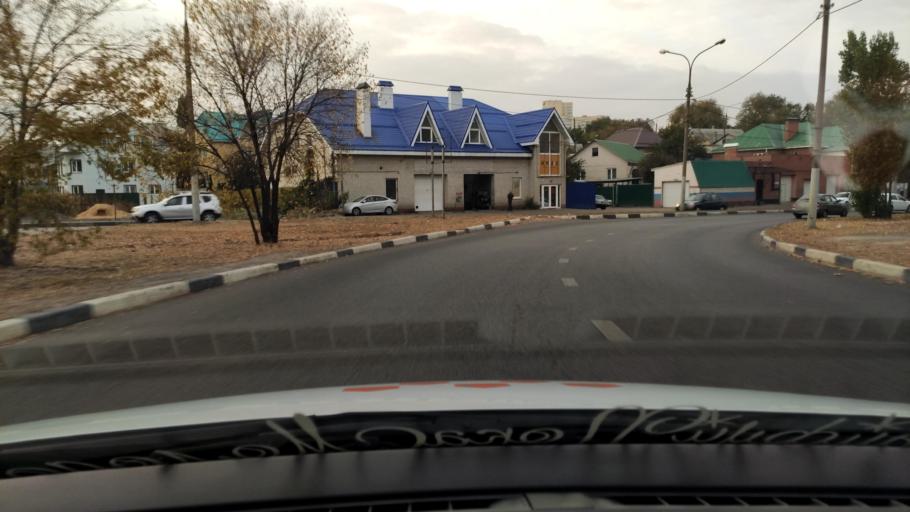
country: RU
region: Voronezj
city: Voronezh
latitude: 51.6359
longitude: 39.2081
